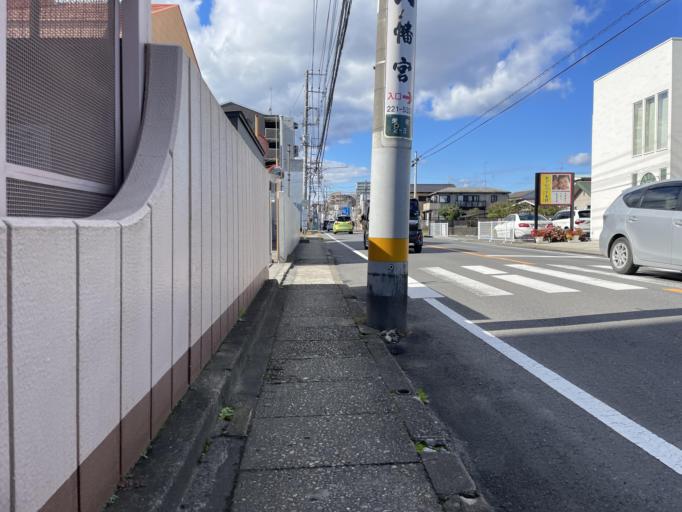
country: JP
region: Ibaraki
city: Mito-shi
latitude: 36.3853
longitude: 140.4592
